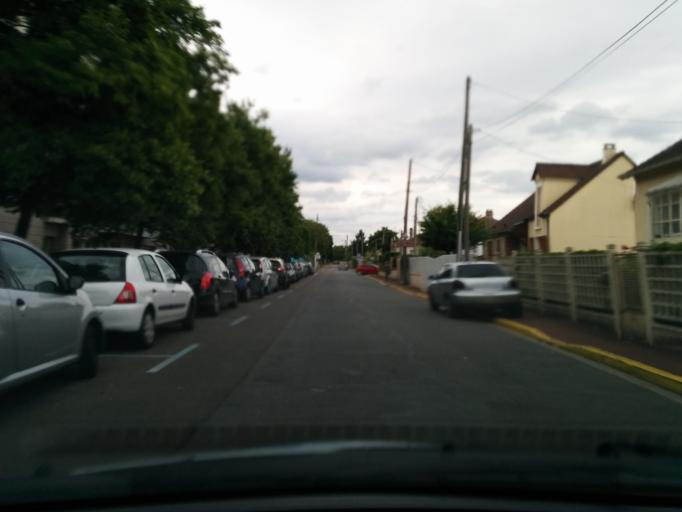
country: FR
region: Ile-de-France
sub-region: Departement des Yvelines
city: Aubergenville
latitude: 48.9715
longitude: 1.8497
